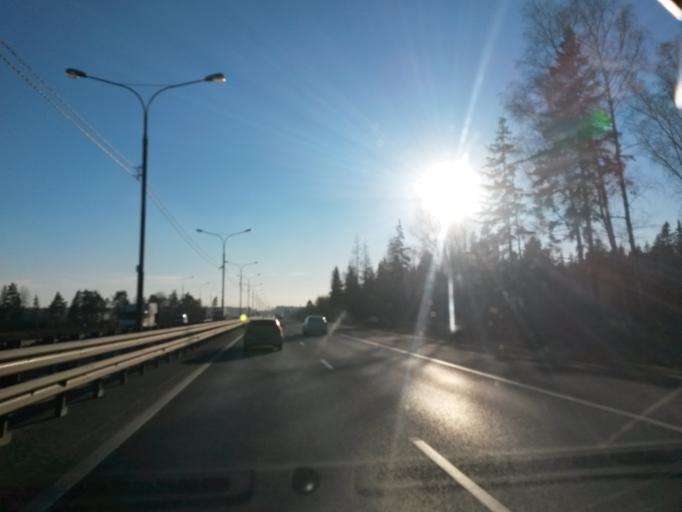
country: RU
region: Moskovskaya
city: Pushkino
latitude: 56.0267
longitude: 37.8853
